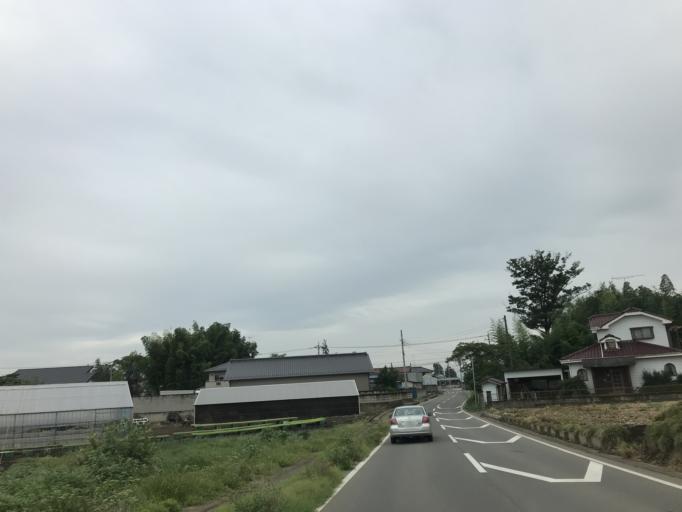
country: JP
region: Ibaraki
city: Sakai
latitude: 36.1498
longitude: 139.7920
